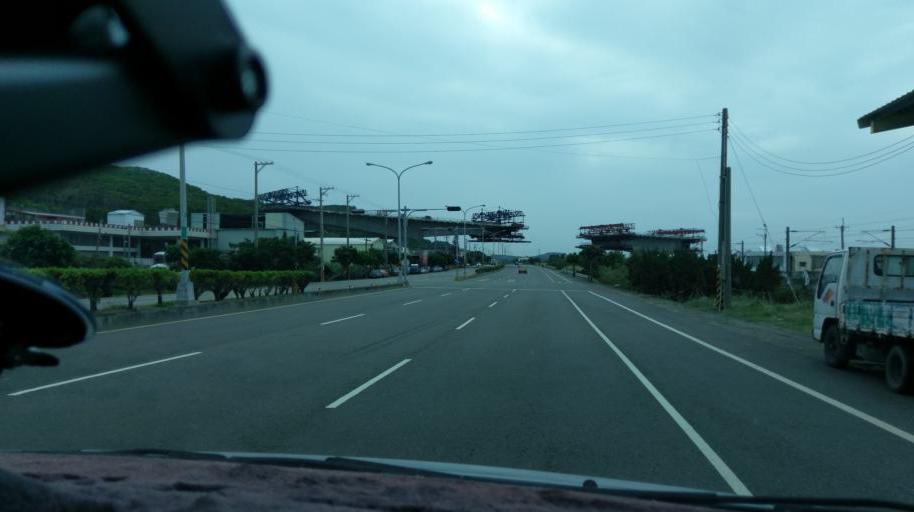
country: TW
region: Taiwan
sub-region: Miaoli
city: Miaoli
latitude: 24.5324
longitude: 120.6937
